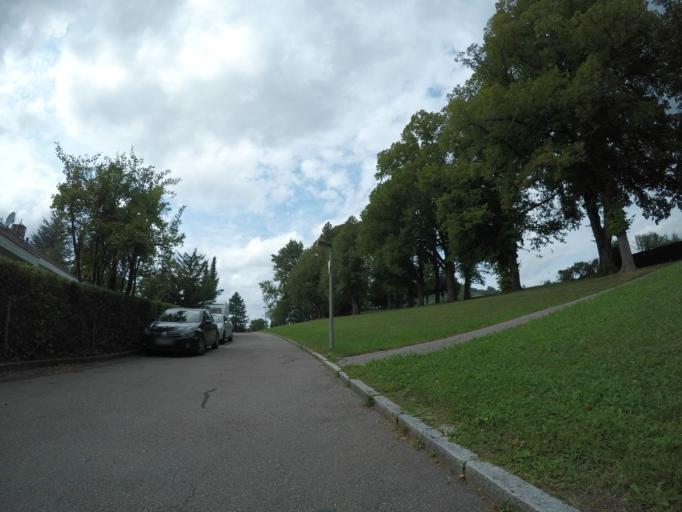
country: DE
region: Baden-Wuerttemberg
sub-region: Tuebingen Region
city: Eningen unter Achalm
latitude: 48.4837
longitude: 9.2419
